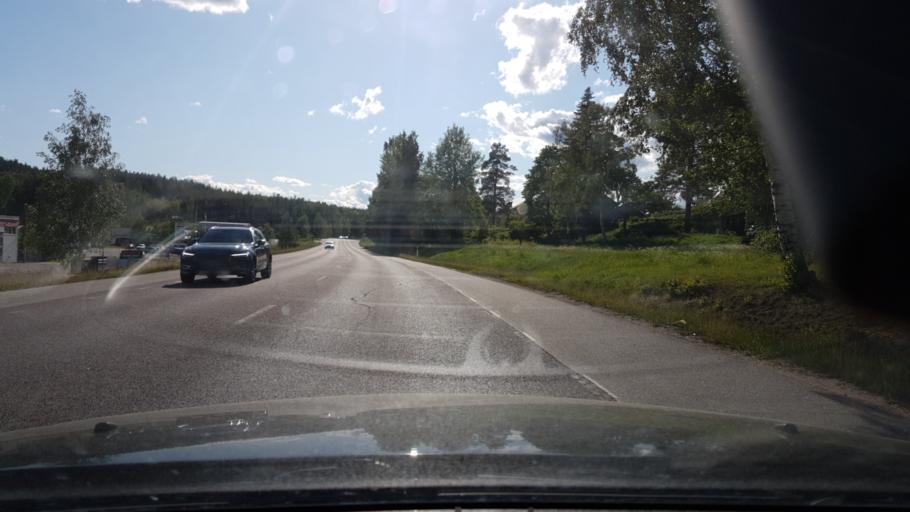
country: SE
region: Gaevleborg
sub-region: Bollnas Kommun
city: Bollnas
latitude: 61.3449
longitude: 16.3775
